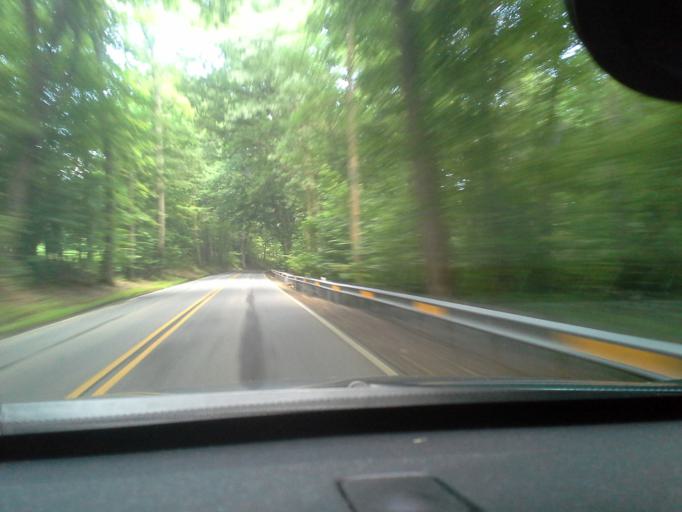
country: US
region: Maryland
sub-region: Calvert County
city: Huntingtown
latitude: 38.6039
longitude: -76.5473
